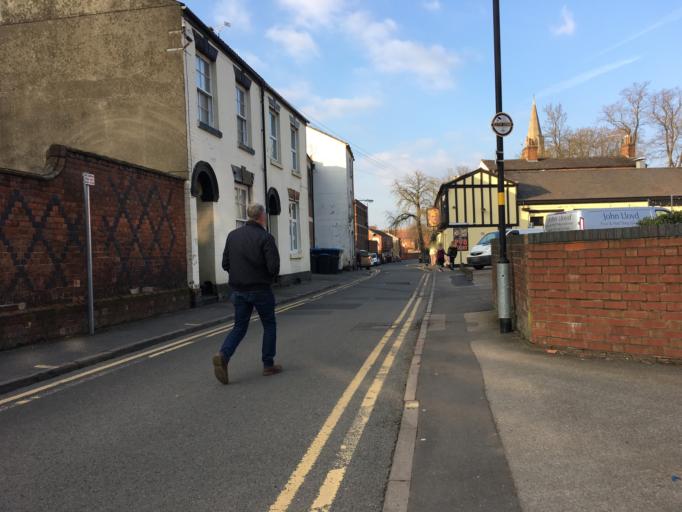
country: GB
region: England
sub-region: Warwickshire
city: Rugby
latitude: 52.3709
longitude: -1.2616
